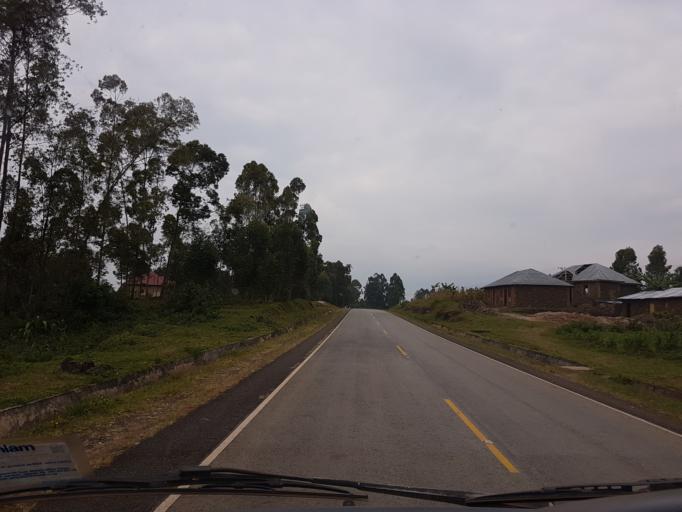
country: UG
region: Western Region
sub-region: Kisoro District
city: Kisoro
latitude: -1.3222
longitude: 29.7287
